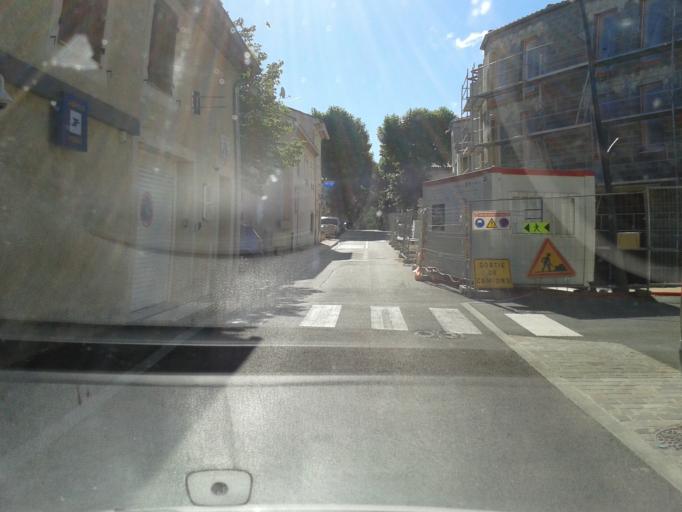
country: FR
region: Provence-Alpes-Cote d'Azur
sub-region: Departement du Vaucluse
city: Beaumont-de-Pertuis
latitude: 43.6873
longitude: 5.7089
